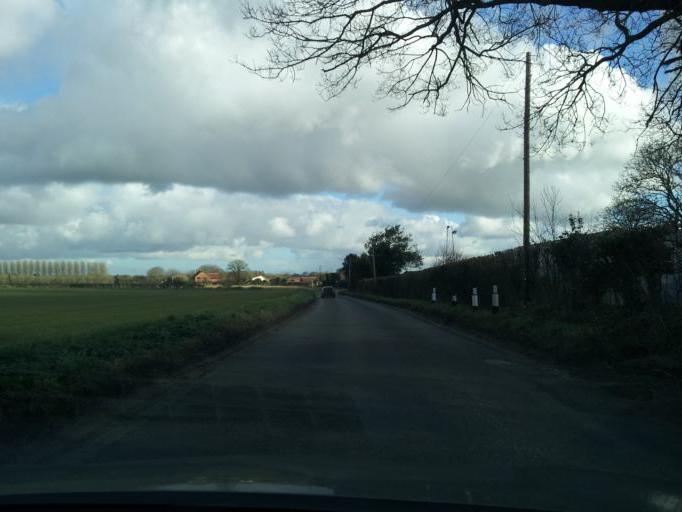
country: GB
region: England
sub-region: Norfolk
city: Mattishall
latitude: 52.6591
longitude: 1.0524
